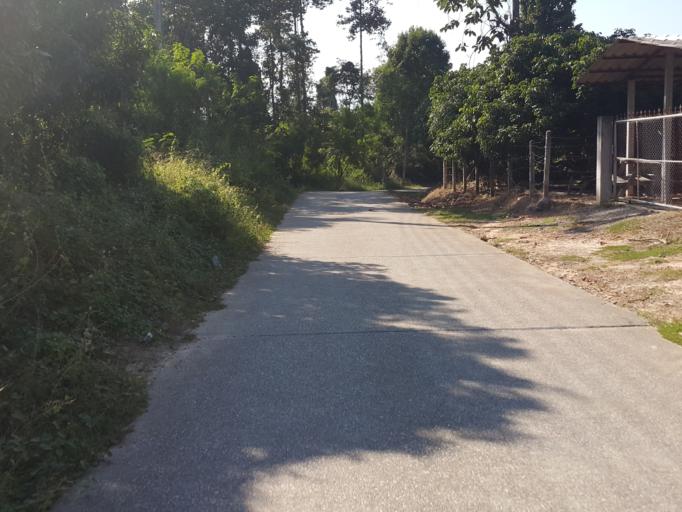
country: TH
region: Chiang Mai
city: Mae On
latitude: 18.7957
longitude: 99.1826
